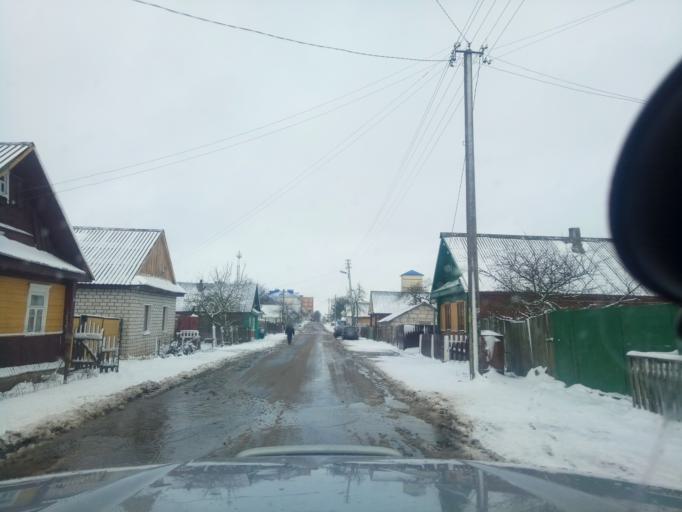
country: BY
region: Minsk
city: Kapyl'
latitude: 53.1543
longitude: 27.0838
